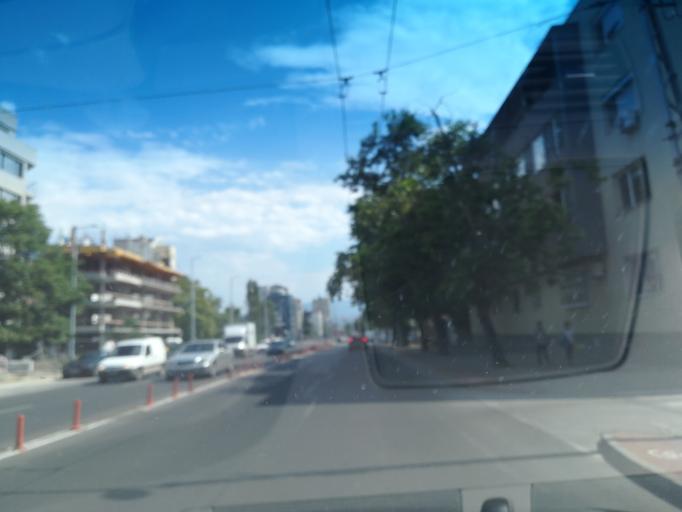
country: BG
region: Plovdiv
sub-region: Obshtina Plovdiv
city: Plovdiv
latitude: 42.1488
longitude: 24.7632
